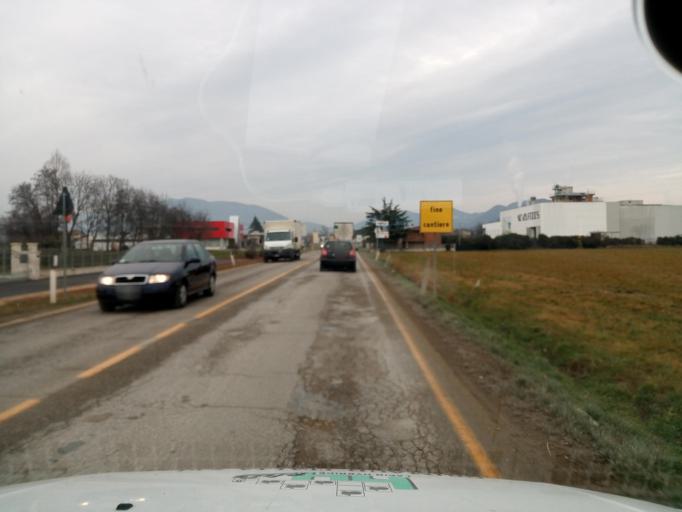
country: IT
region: Veneto
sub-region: Provincia di Vicenza
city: Castelgomberto
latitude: 45.5718
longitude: 11.3838
